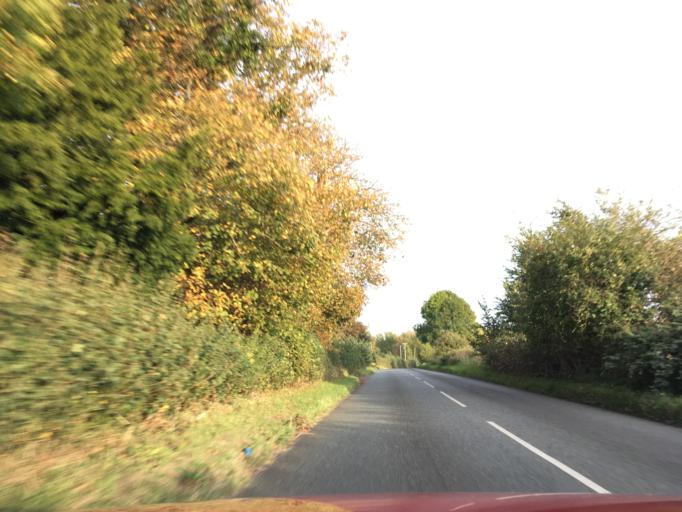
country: GB
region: England
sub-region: South Gloucestershire
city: Almondsbury
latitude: 51.5914
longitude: -2.5878
